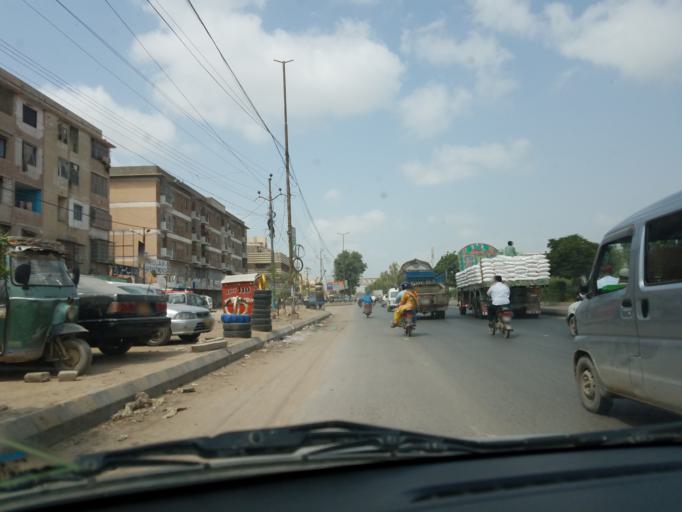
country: PK
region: Sindh
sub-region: Karachi District
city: Karachi
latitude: 24.9481
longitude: 67.0822
